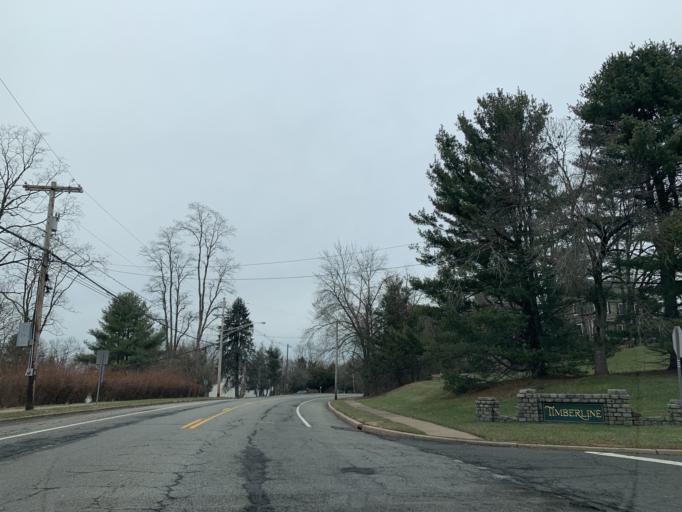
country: US
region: New Jersey
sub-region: Somerset County
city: Green Knoll
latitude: 40.6333
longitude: -74.6091
